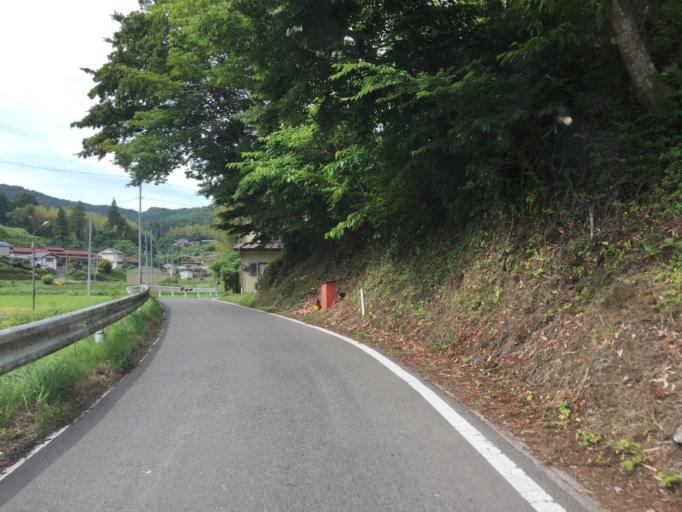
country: JP
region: Fukushima
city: Funehikimachi-funehiki
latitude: 37.4552
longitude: 140.6410
